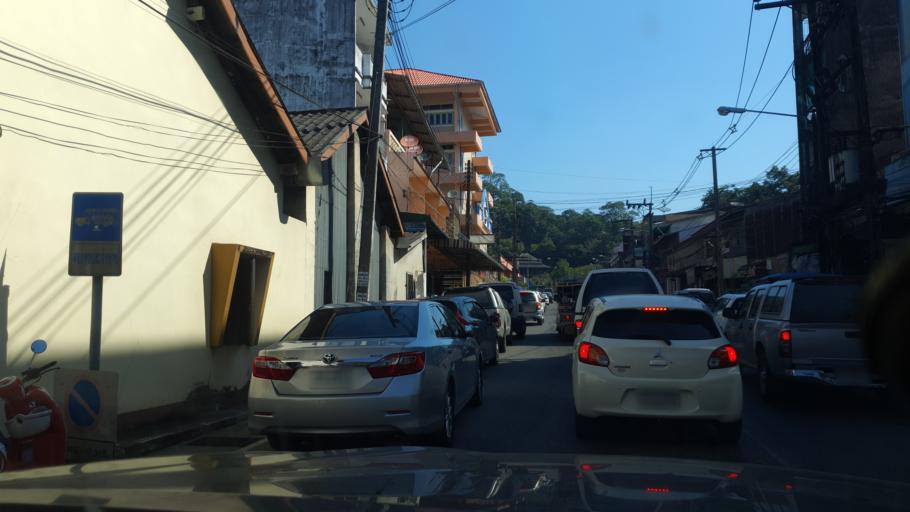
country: TH
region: Ranong
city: Ranong
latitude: 9.9642
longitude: 98.6342
